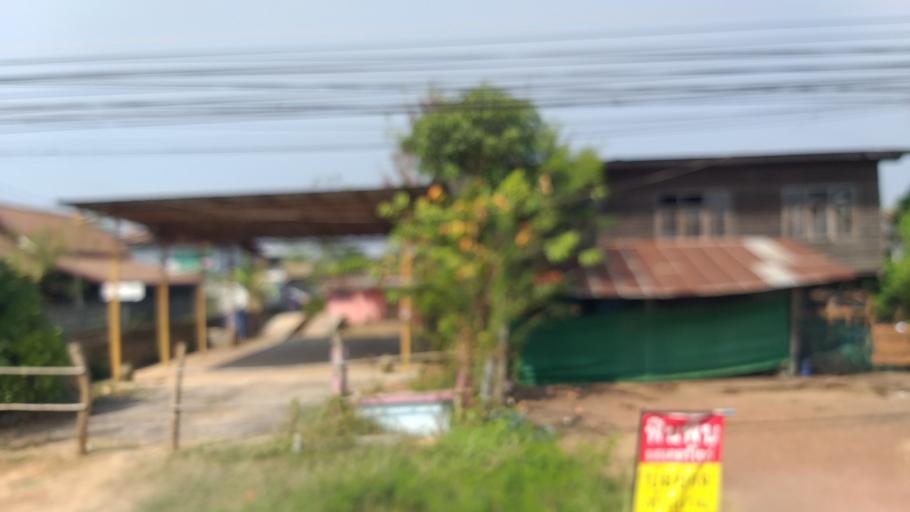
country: TH
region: Changwat Udon Thani
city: Nong Han
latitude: 17.3638
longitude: 102.9801
